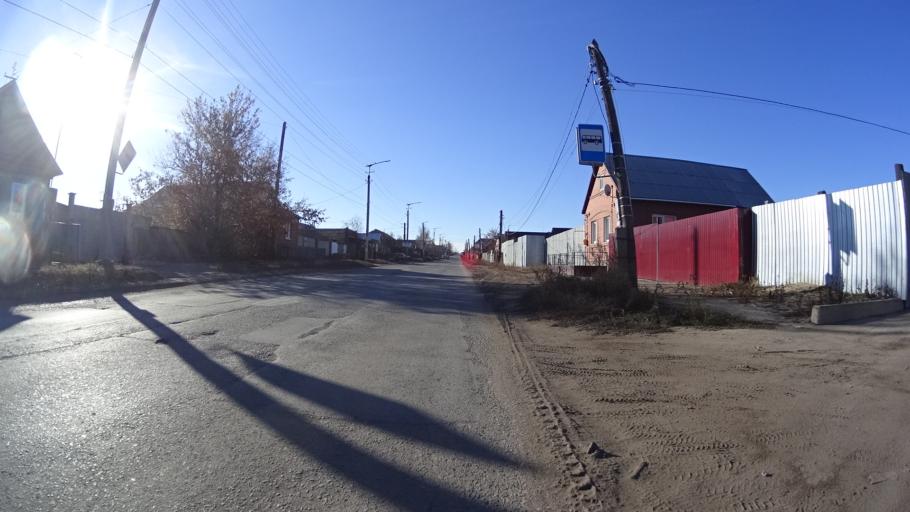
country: RU
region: Chelyabinsk
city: Troitsk
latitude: 54.0899
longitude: 61.5406
